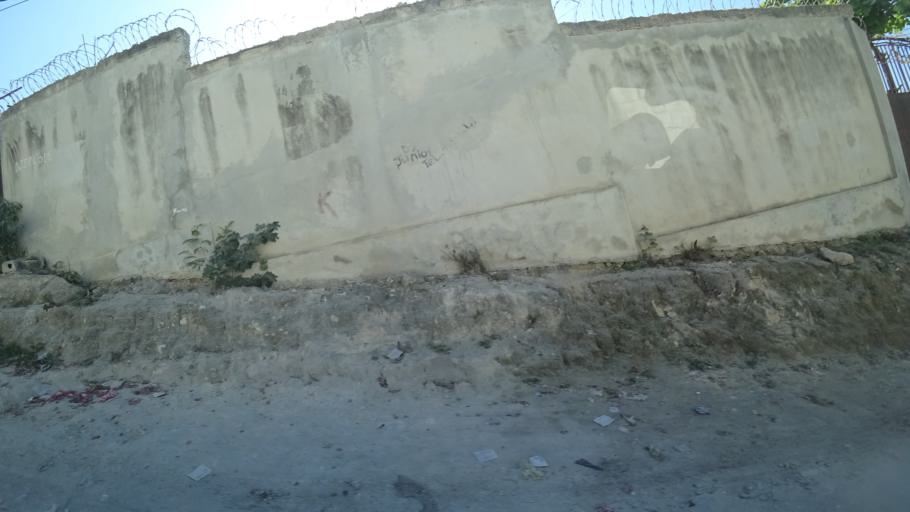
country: HT
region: Ouest
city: Delmas 73
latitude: 18.5581
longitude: -72.2867
